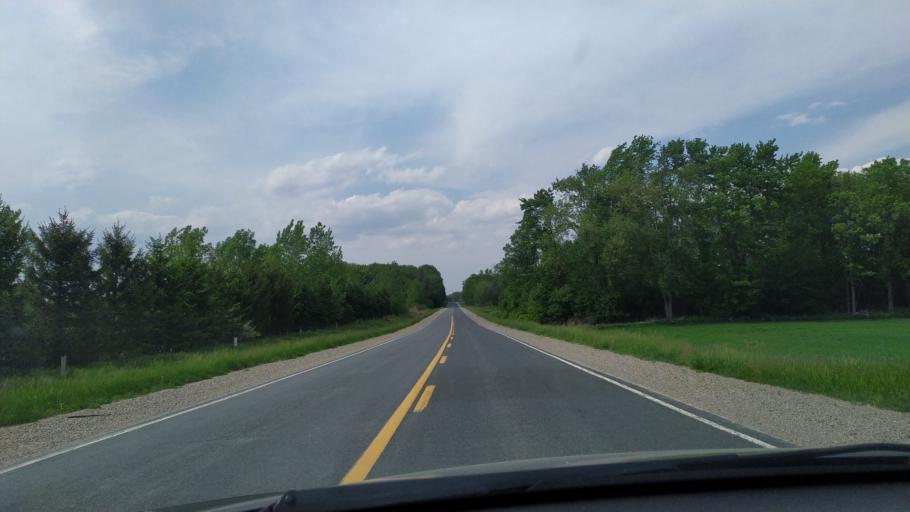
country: CA
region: Ontario
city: Ingersoll
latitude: 43.0393
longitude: -80.9776
